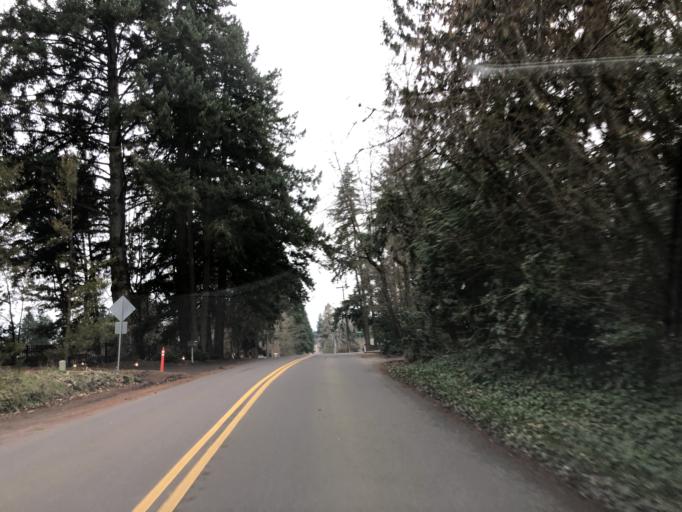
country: US
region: Oregon
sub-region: Washington County
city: Tigard
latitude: 45.4267
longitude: -122.7952
